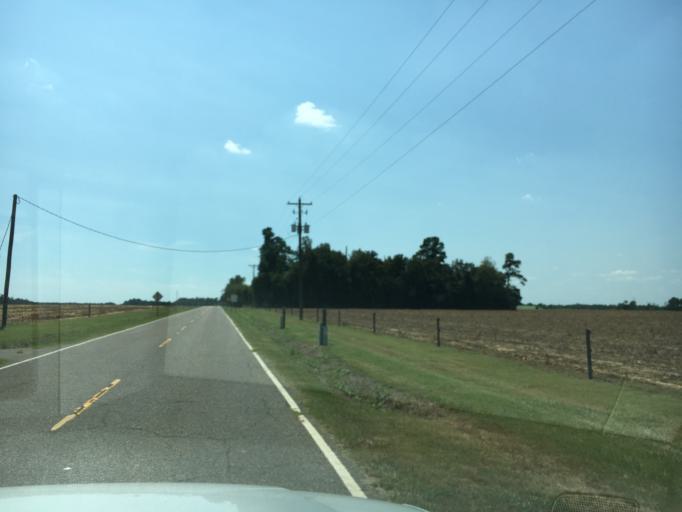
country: US
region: South Carolina
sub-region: Lexington County
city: Batesburg
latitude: 33.8383
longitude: -81.6622
